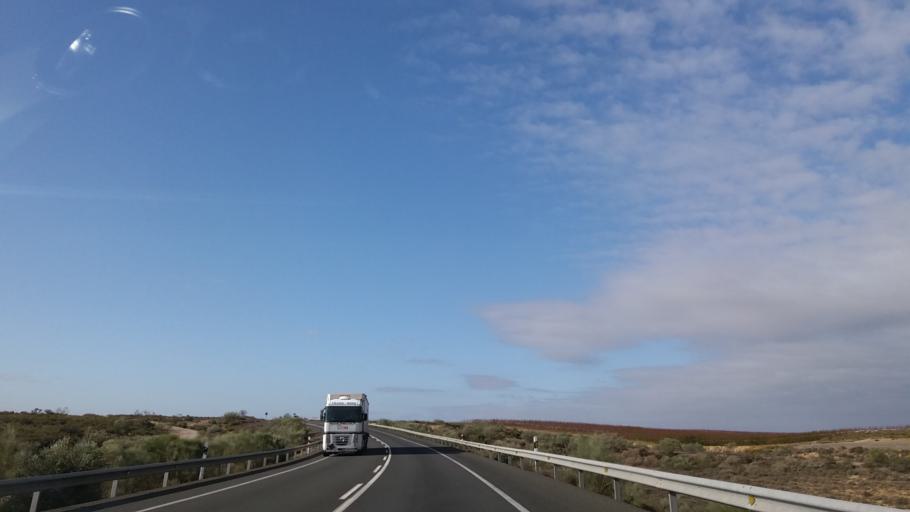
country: ES
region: Aragon
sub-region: Provincia de Huesca
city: Candasnos
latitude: 41.5197
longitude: 0.1239
